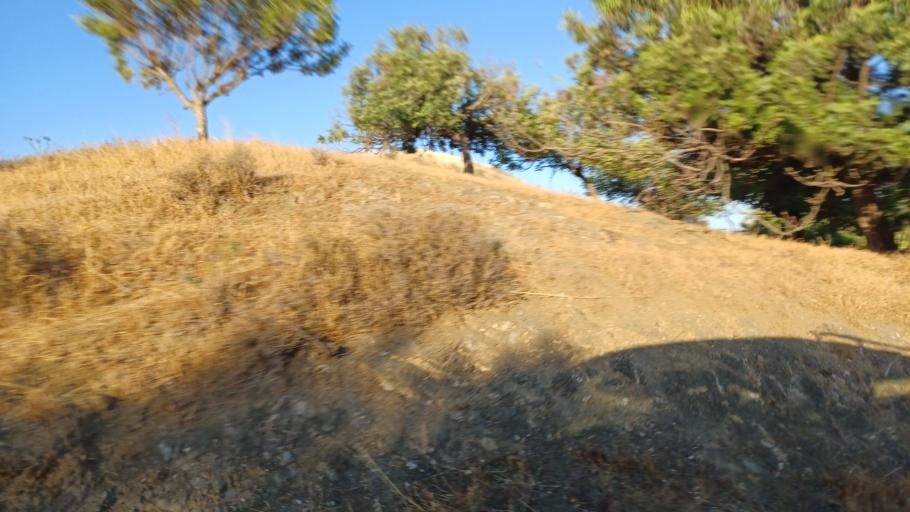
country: CY
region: Larnaka
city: Troulloi
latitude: 35.0298
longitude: 33.6416
